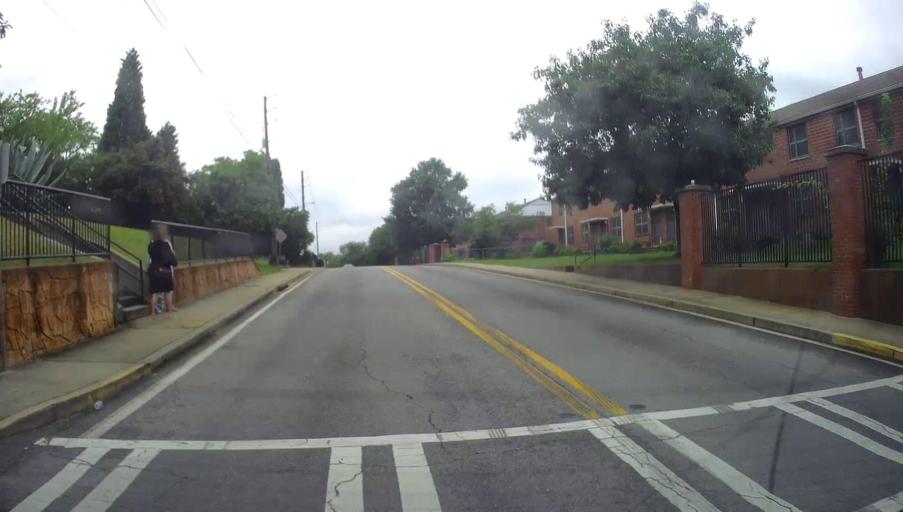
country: US
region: Georgia
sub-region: Bibb County
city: Macon
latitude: 32.8176
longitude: -83.6423
